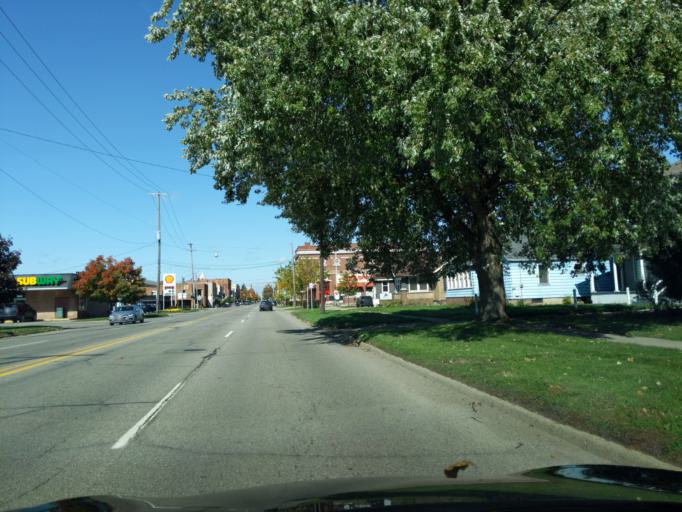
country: US
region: Michigan
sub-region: Eaton County
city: Charlotte
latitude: 42.5594
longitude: -84.8358
